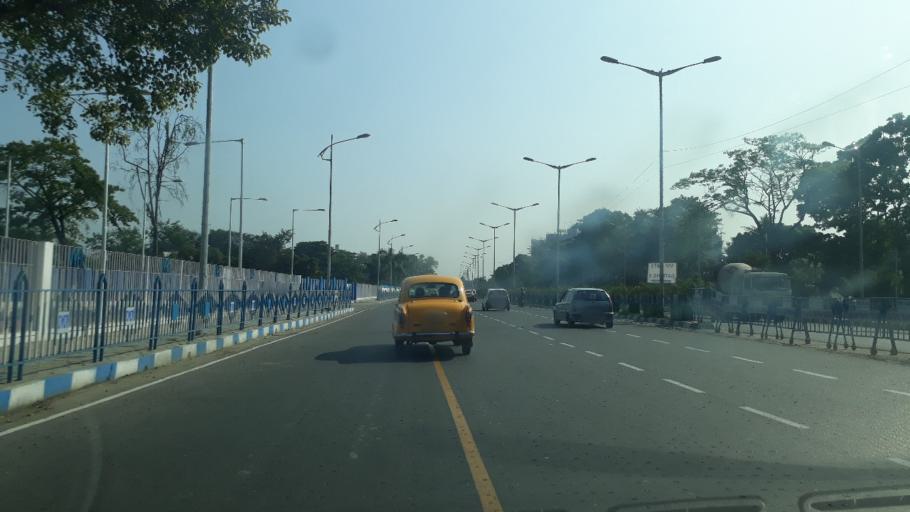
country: IN
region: West Bengal
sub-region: Kolkata
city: Kolkata
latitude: 22.5684
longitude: 88.4055
